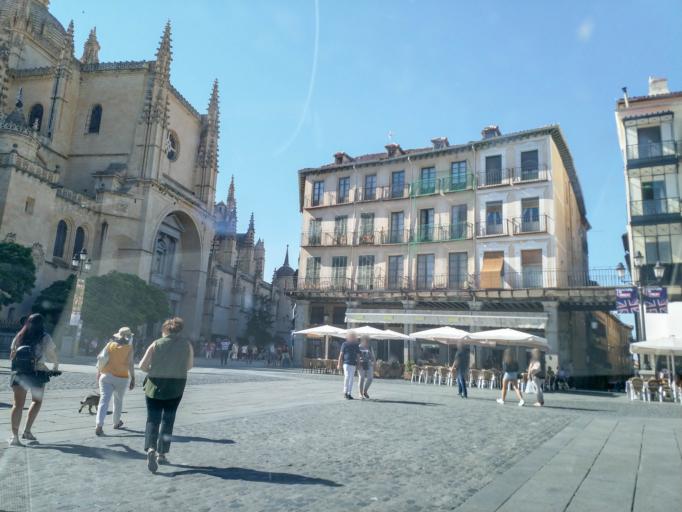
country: ES
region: Castille and Leon
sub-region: Provincia de Segovia
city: Segovia
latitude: 40.9502
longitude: -4.1242
